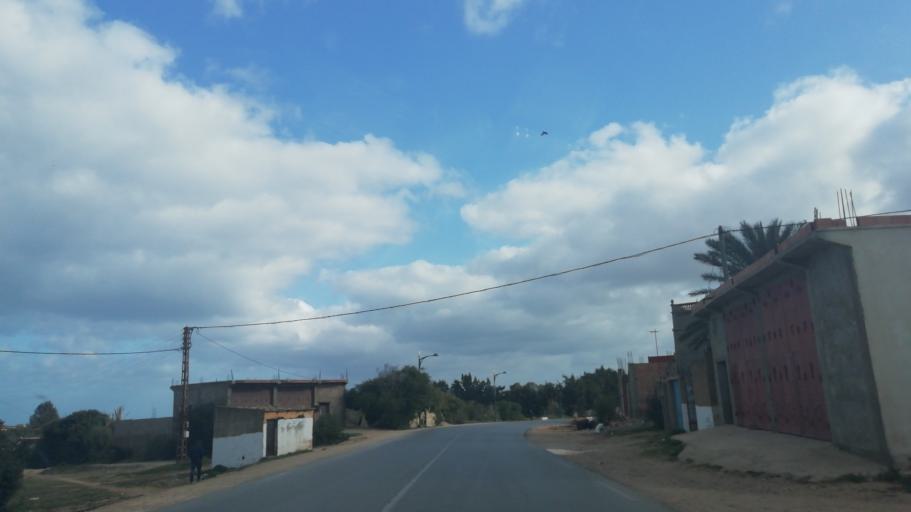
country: DZ
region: Relizane
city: Mazouna
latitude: 36.2787
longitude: 0.6376
